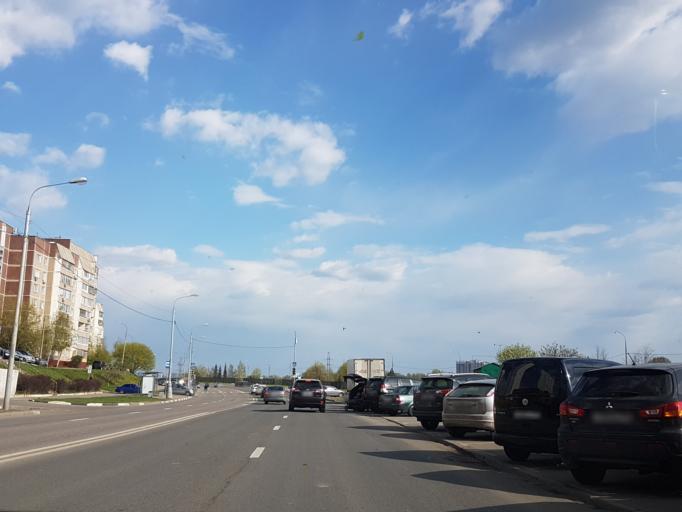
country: RU
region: Moskovskaya
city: Pavshino
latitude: 55.8408
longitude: 37.3571
